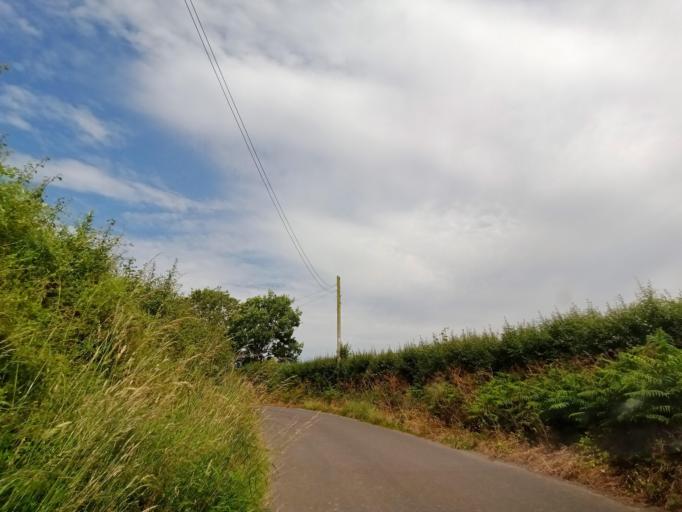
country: IE
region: Leinster
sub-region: Kilkenny
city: Thomastown
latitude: 52.5721
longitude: -7.1257
